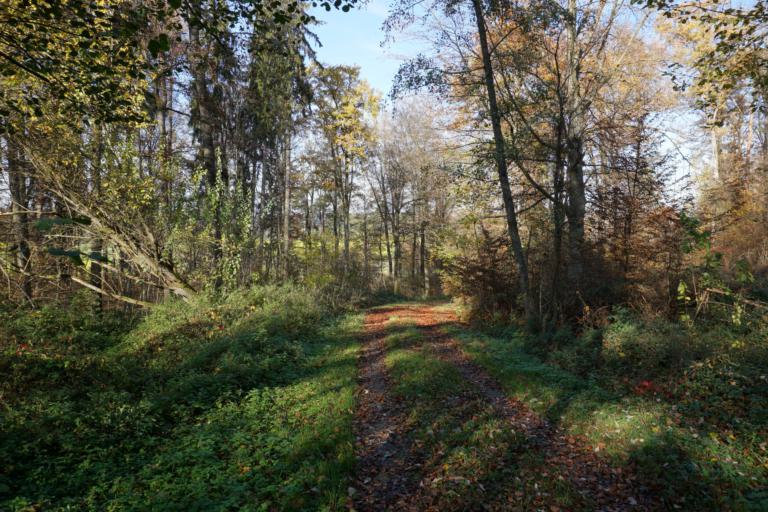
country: DE
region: Baden-Wuerttemberg
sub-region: Karlsruhe Region
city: Aglasterhausen
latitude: 49.3664
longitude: 8.9972
